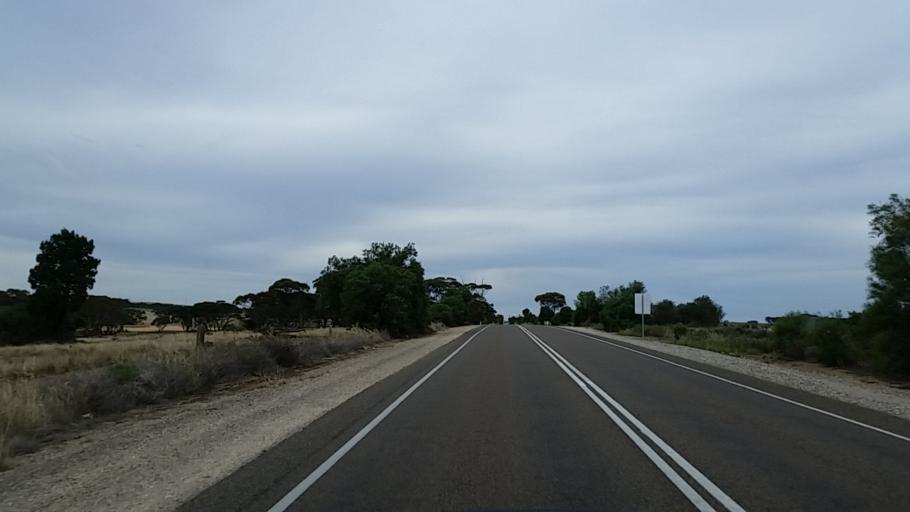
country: AU
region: South Australia
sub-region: Mid Murray
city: Mannum
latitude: -34.9303
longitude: 139.2437
